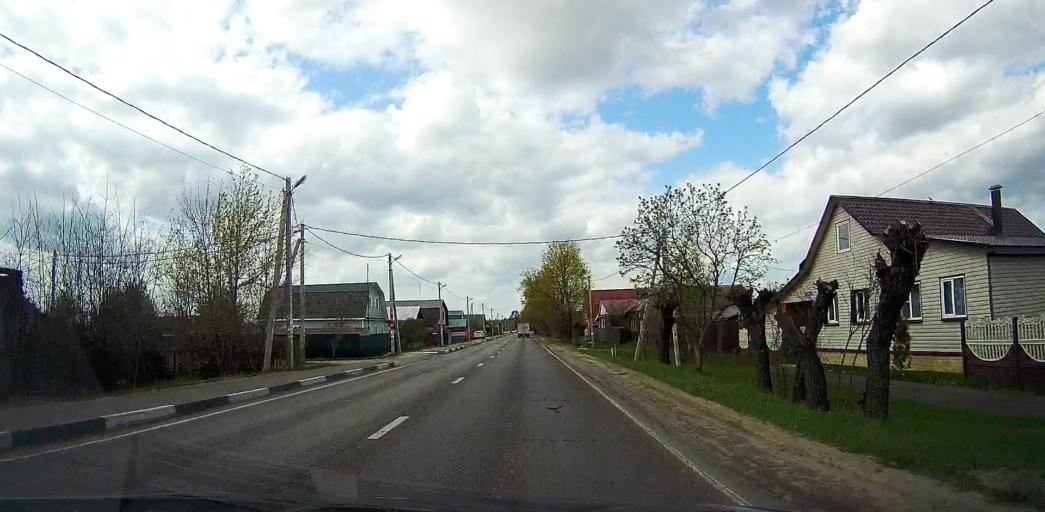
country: RU
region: Moskovskaya
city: Davydovo
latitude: 55.6385
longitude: 38.8651
